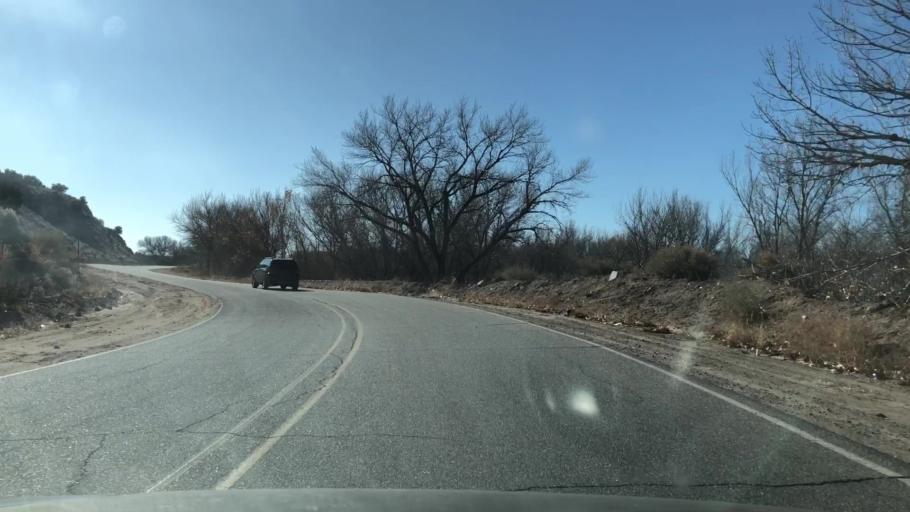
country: US
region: New Mexico
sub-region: Rio Arriba County
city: Ohkay Owingeh
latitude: 36.0946
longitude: -106.1298
